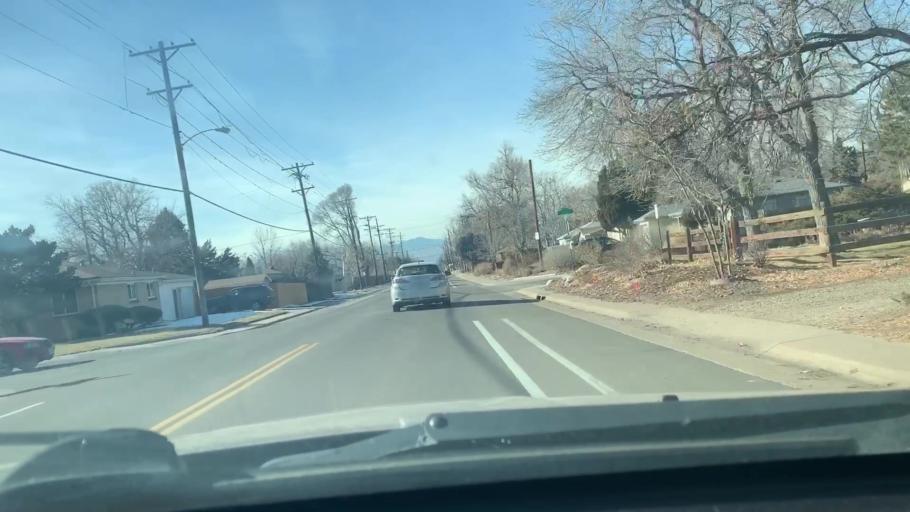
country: US
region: Colorado
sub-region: Arapahoe County
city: Glendale
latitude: 39.6894
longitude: -104.9358
